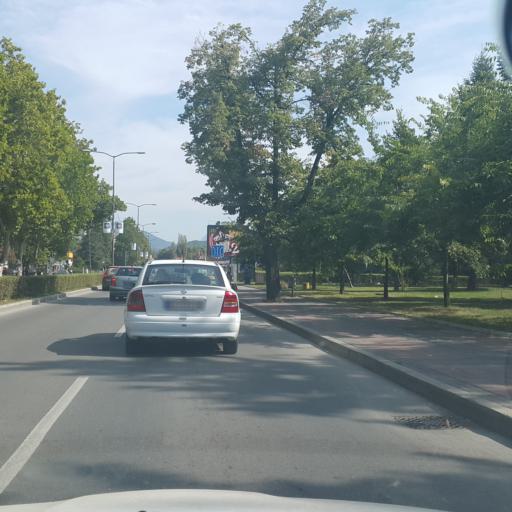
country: RS
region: Central Serbia
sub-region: Nisavski Okrug
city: Nis
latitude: 43.3161
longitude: 21.9148
